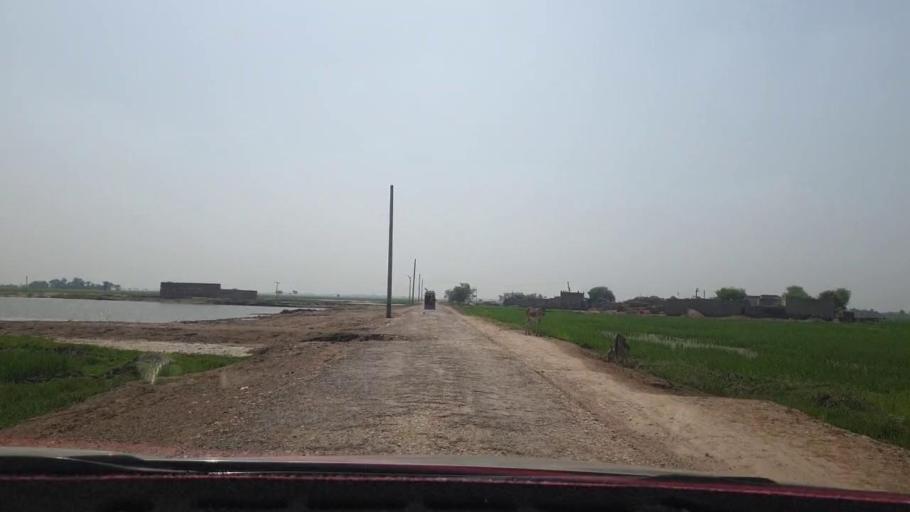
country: PK
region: Sindh
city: Warah
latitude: 27.4055
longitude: 67.8460
